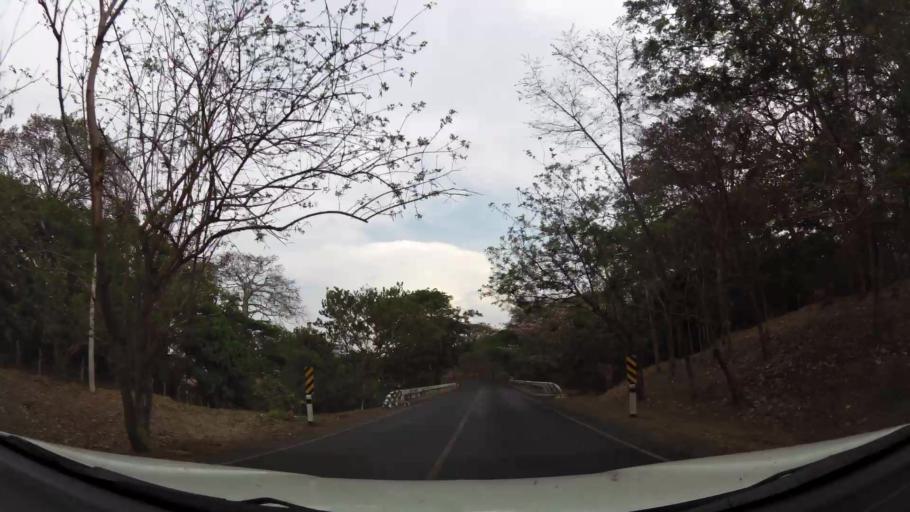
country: NI
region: Rivas
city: Cardenas
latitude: 11.2763
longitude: -85.6605
